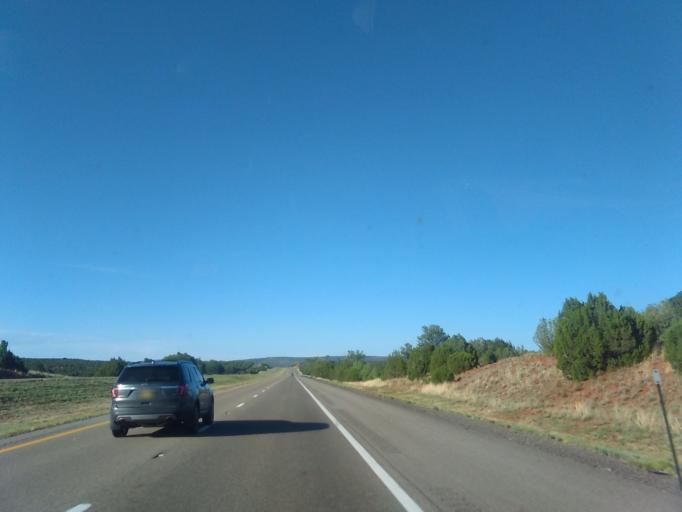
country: US
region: New Mexico
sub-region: San Miguel County
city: Las Vegas
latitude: 35.4350
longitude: -105.2907
